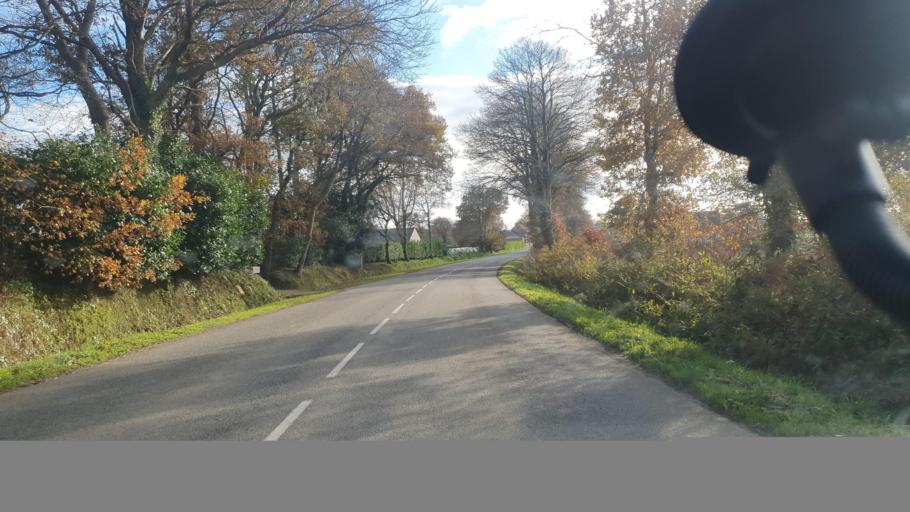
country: FR
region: Brittany
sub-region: Departement du Finistere
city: Briec
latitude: 48.0670
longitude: -4.0196
